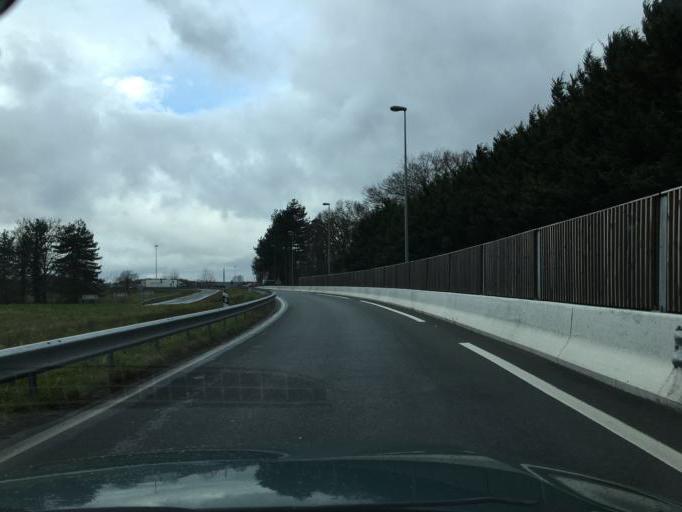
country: FR
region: Centre
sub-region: Departement du Loiret
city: Saran
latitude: 47.9487
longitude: 1.8679
